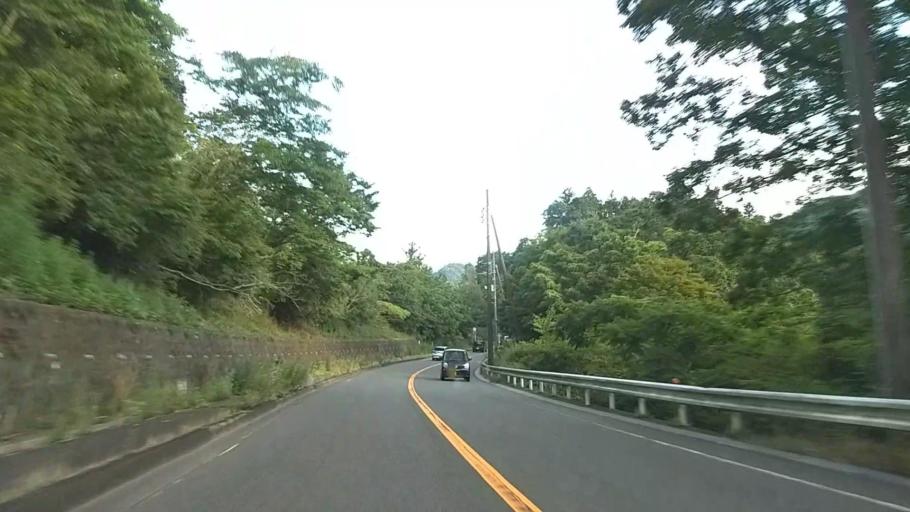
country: JP
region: Yamanashi
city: Uenohara
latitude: 35.5290
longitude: 139.2227
